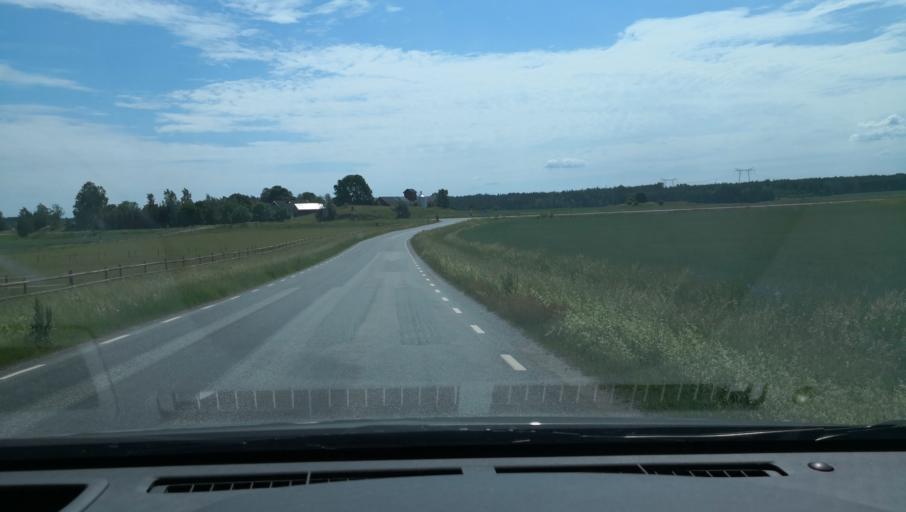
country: SE
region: Uppsala
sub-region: Habo Kommun
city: Balsta
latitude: 59.6396
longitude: 17.4641
